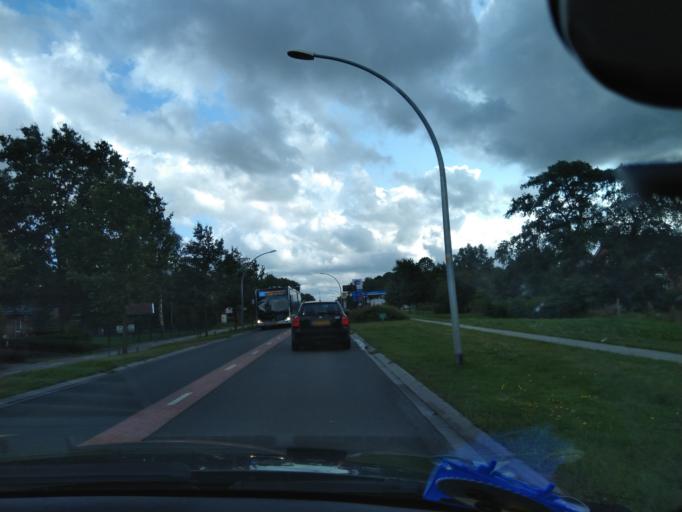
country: NL
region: Groningen
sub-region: Gemeente Groningen
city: Groningen
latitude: 53.1944
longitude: 6.5113
